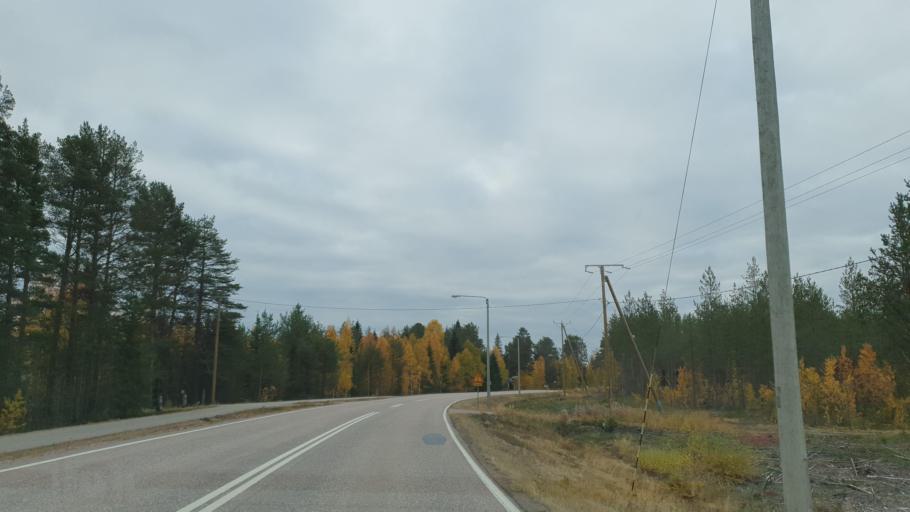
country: FI
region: Lapland
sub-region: Rovaniemi
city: Rovaniemi
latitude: 66.8627
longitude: 25.4643
